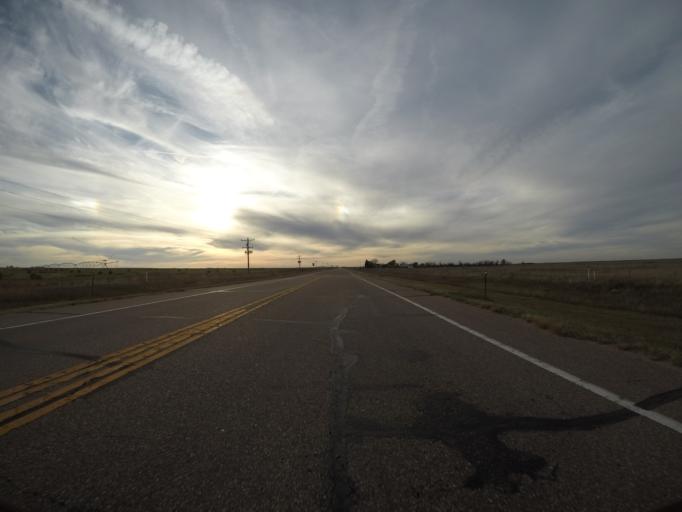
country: US
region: Colorado
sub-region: Yuma County
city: Yuma
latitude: 39.6561
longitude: -102.6898
